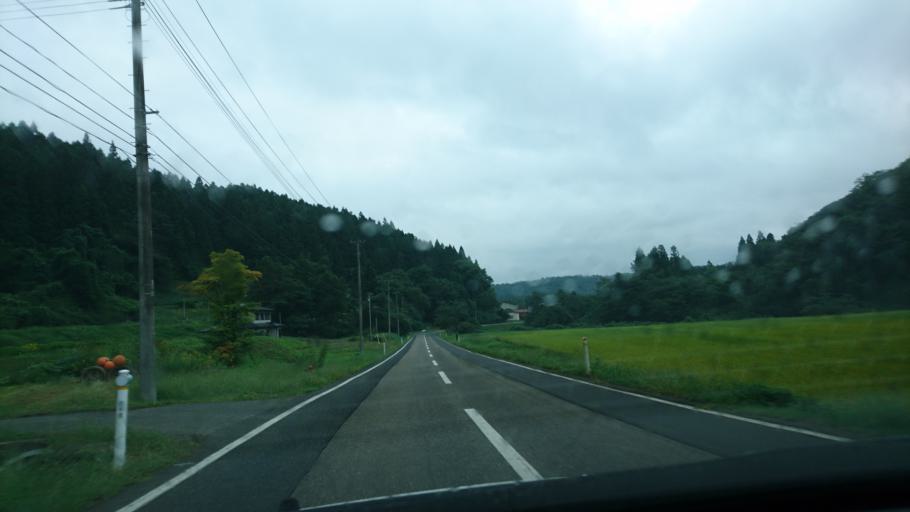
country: JP
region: Iwate
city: Ichinoseki
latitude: 38.9036
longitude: 141.0435
